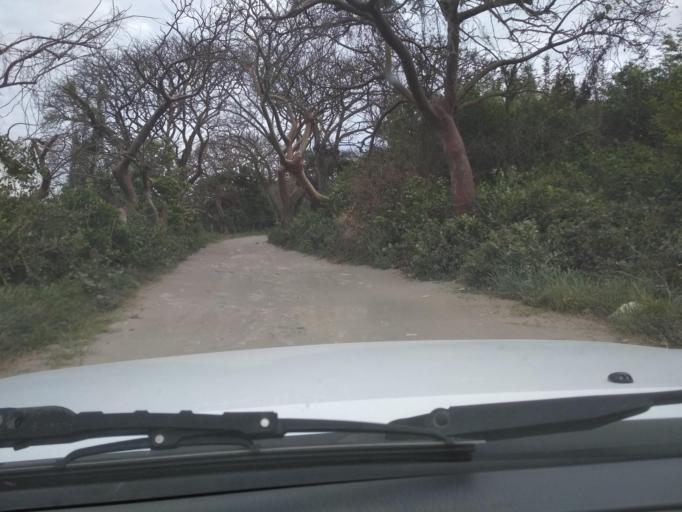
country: MX
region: Veracruz
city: Anton Lizardo
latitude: 19.0562
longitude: -95.9920
